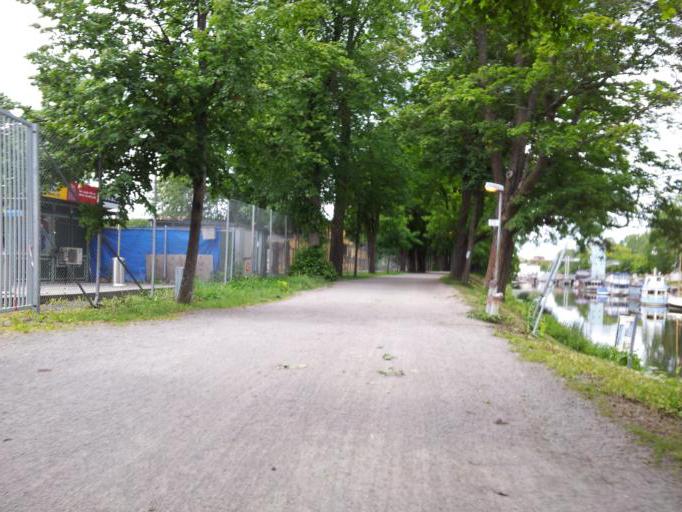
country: SE
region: Uppsala
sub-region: Uppsala Kommun
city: Uppsala
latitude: 59.8490
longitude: 17.6478
